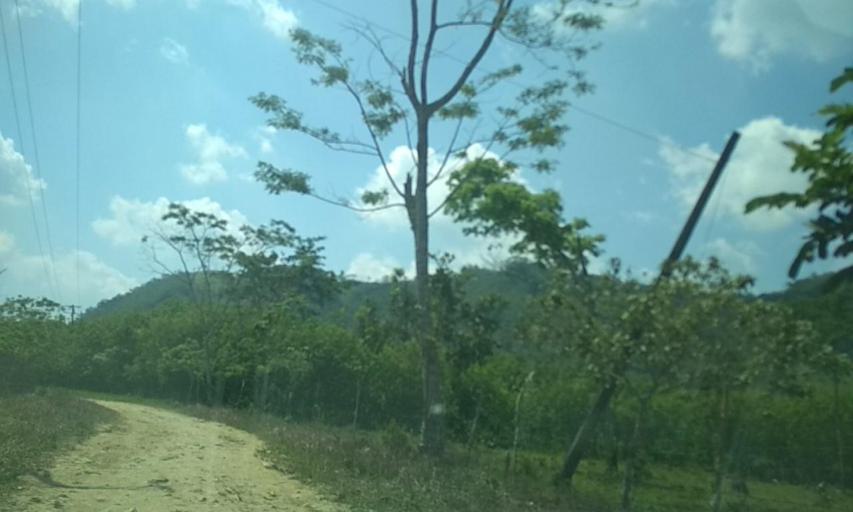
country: MX
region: Chiapas
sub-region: Tecpatan
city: Raudales Malpaso
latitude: 17.2998
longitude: -93.8156
